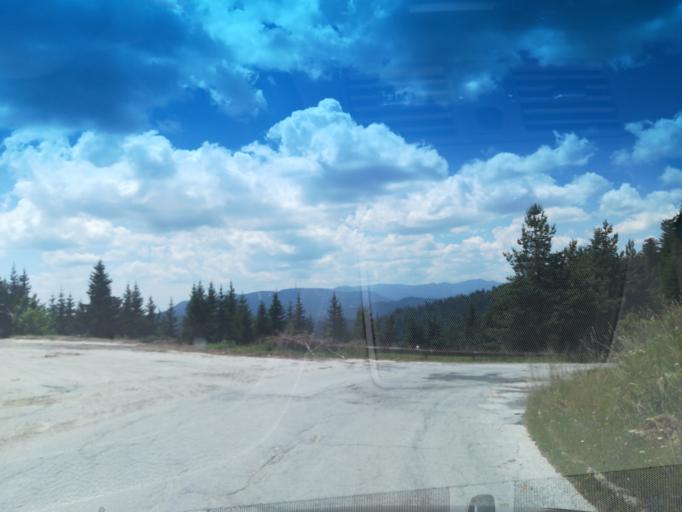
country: BG
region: Smolyan
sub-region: Obshtina Chepelare
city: Chepelare
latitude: 41.6927
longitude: 24.7679
